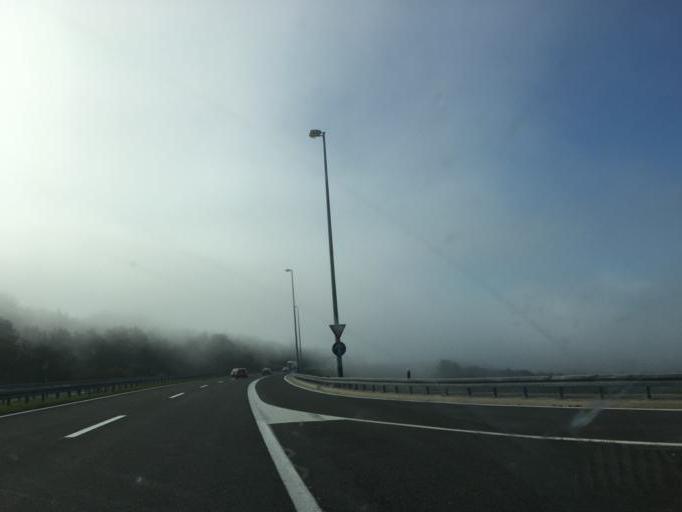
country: HR
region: Licko-Senjska
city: Brinje
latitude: 45.0664
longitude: 15.2077
